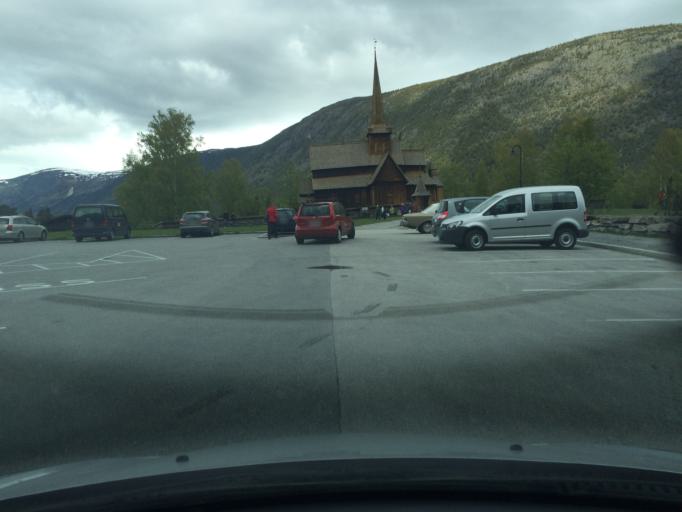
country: NO
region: Oppland
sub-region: Lom
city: Fossbergom
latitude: 61.8388
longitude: 8.5667
